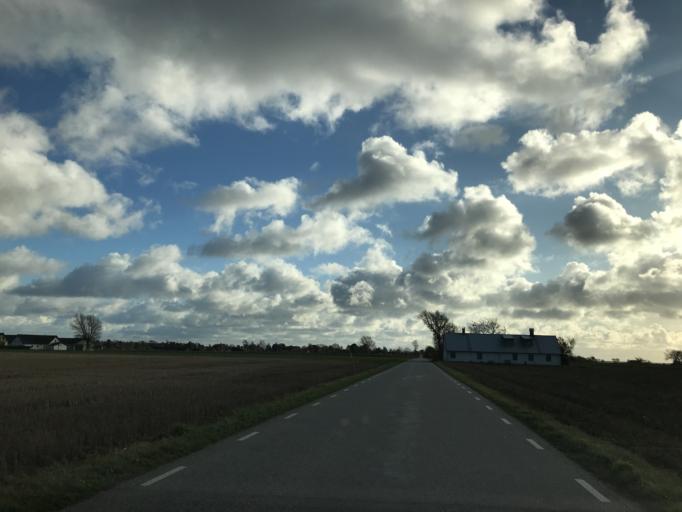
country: SE
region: Skane
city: Smygehamn
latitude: 55.3684
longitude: 13.4136
